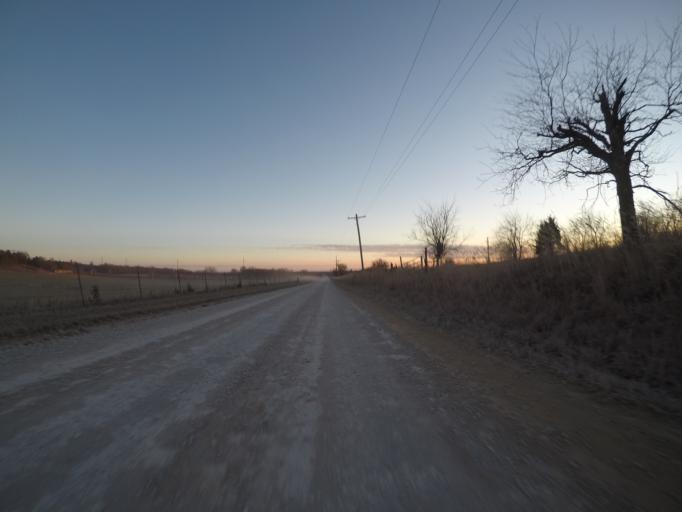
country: US
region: Kansas
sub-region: Riley County
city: Manhattan
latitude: 39.2373
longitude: -96.4827
